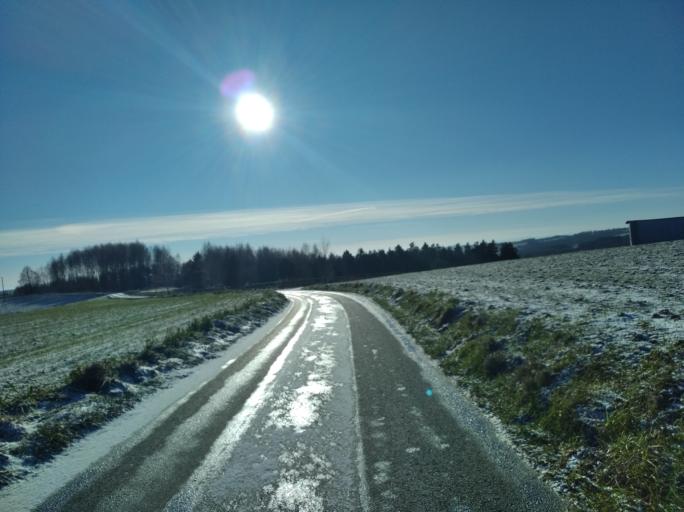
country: PL
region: Subcarpathian Voivodeship
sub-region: Powiat ropczycko-sedziszowski
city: Iwierzyce
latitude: 49.9672
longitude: 21.7494
